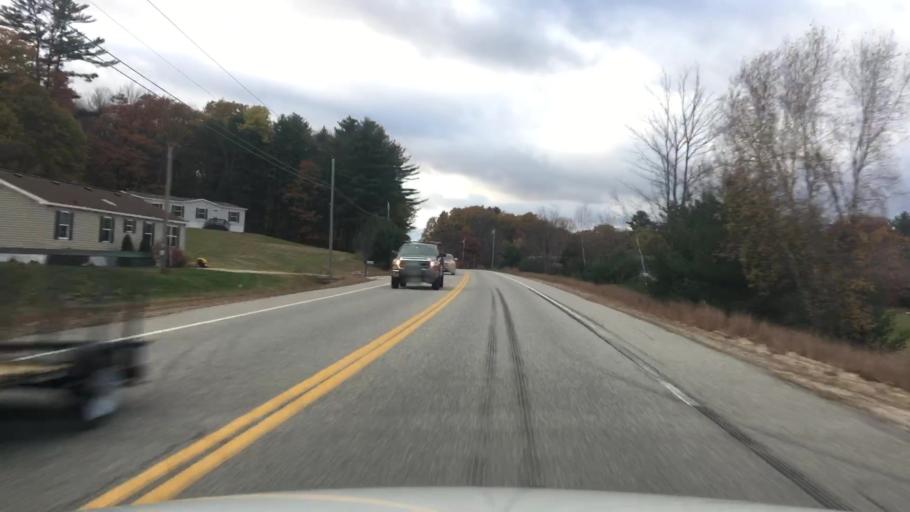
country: US
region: Maine
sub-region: Androscoggin County
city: Livermore
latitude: 44.4128
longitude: -70.2816
